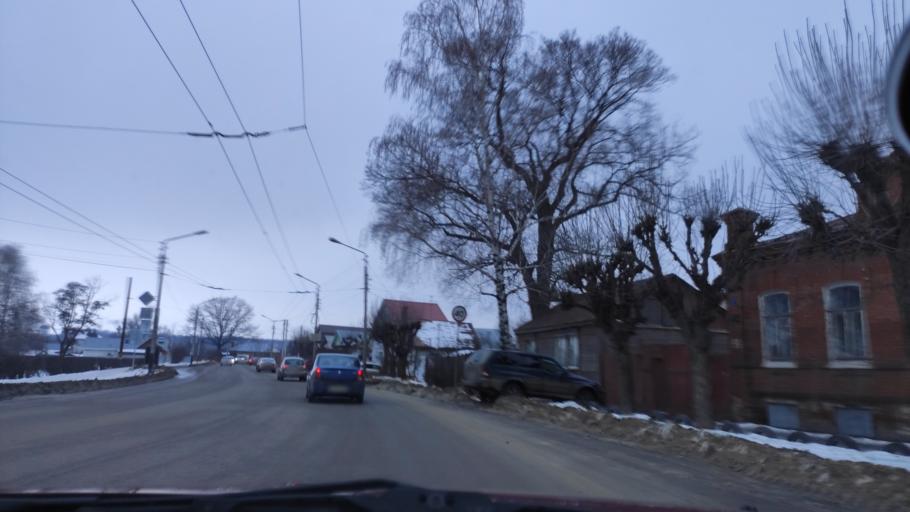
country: RU
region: Tambov
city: Tambov
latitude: 52.7041
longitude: 41.4573
